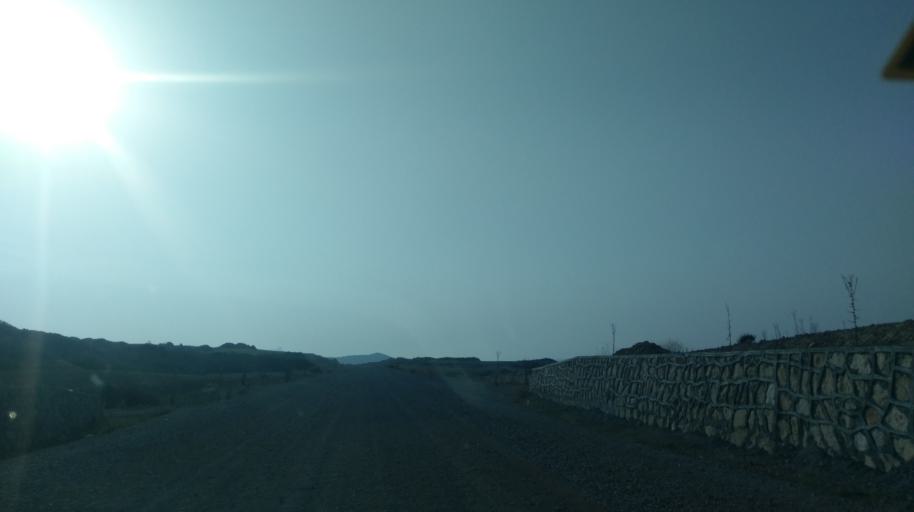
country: CY
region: Ammochostos
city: Leonarisso
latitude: 35.4982
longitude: 34.1084
